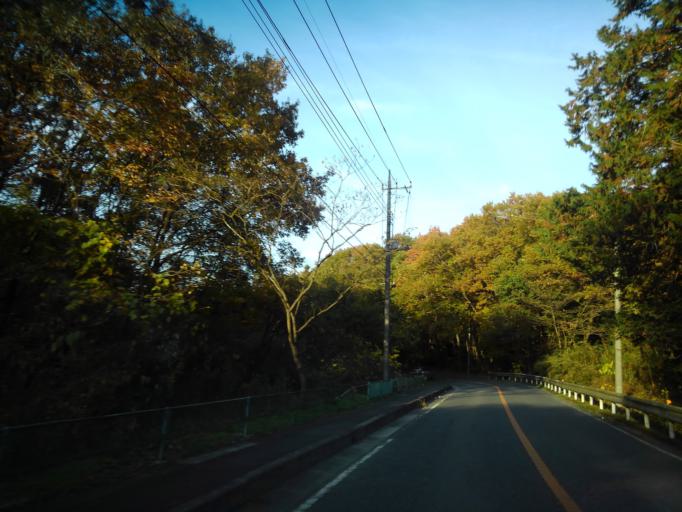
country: JP
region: Saitama
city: Hanno
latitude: 35.8281
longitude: 139.3386
